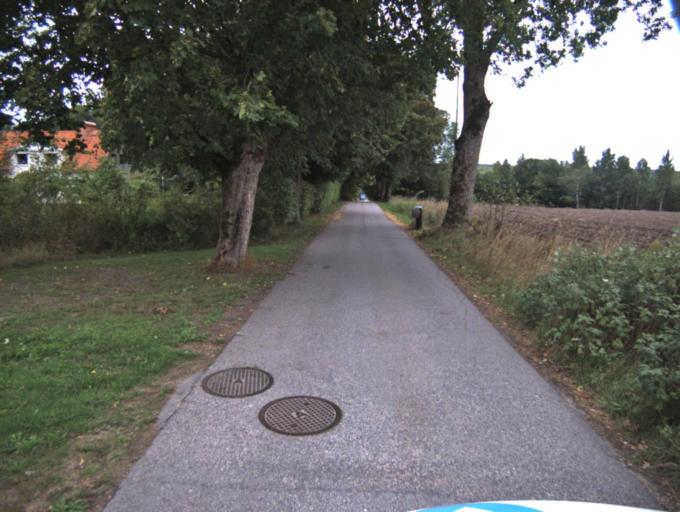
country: SE
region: Vaestra Goetaland
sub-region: Ulricehamns Kommun
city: Ulricehamn
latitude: 57.8403
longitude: 13.2928
